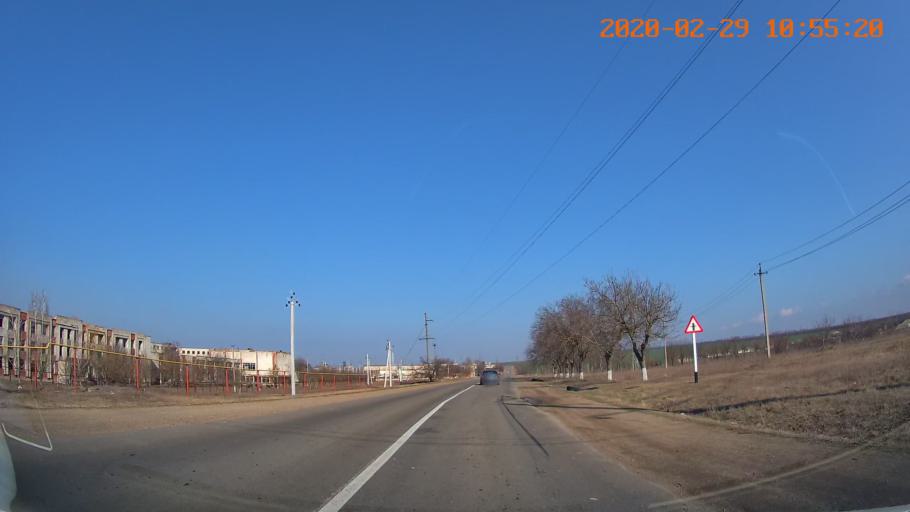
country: MD
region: Telenesti
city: Grigoriopol
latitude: 47.1327
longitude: 29.3249
